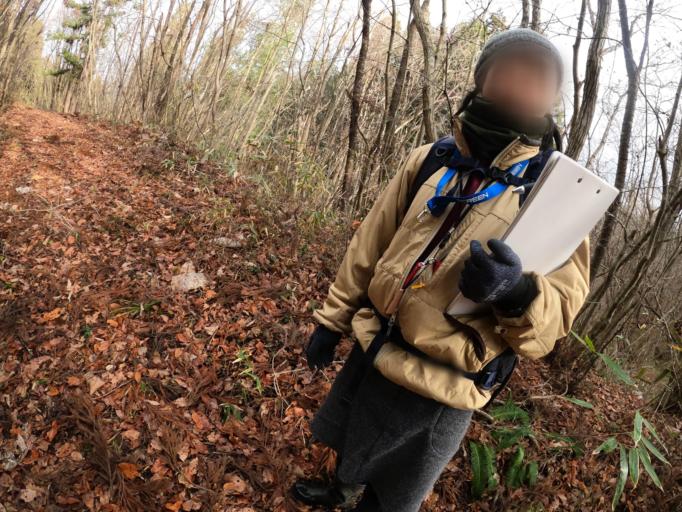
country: JP
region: Iwate
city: Ichinoseki
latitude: 38.8829
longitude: 141.1309
